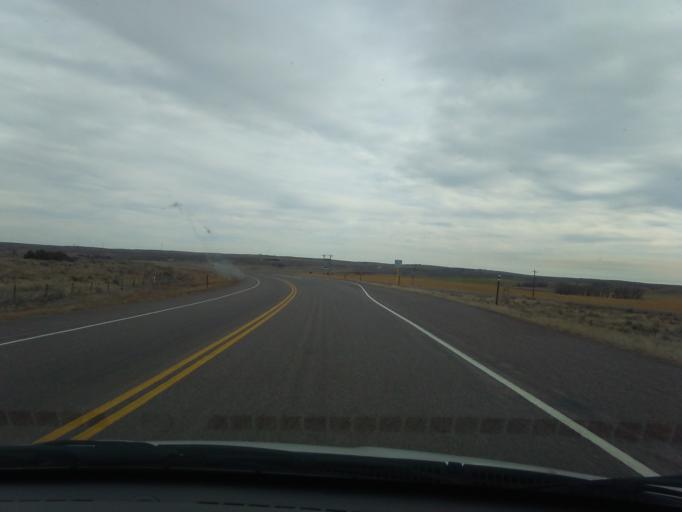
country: US
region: Colorado
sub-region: Yuma County
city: Wray
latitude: 40.0787
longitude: -102.3184
